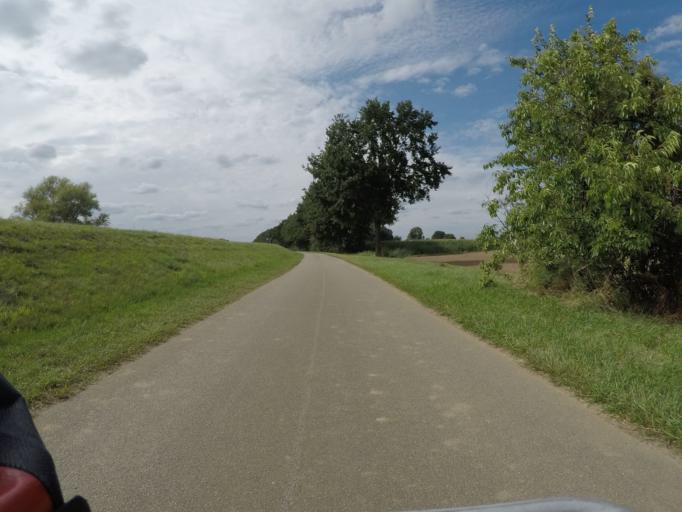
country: DE
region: Lower Saxony
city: Wittorf
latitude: 53.3489
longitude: 10.3810
